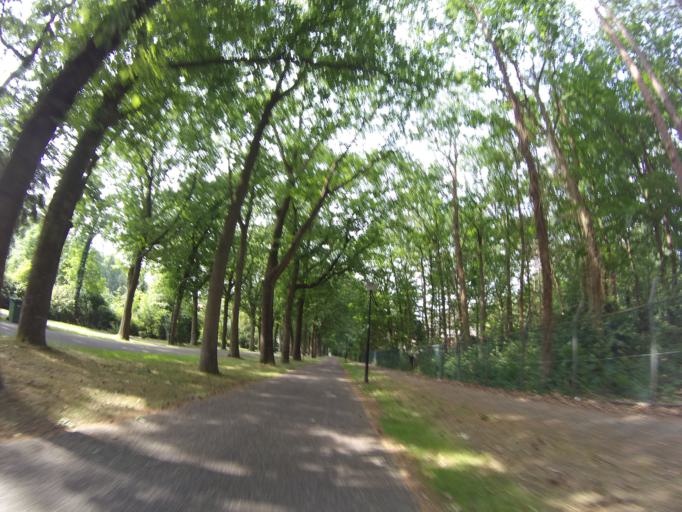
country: NL
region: Utrecht
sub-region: Gemeente Zeist
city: Zeist
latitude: 52.0965
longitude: 5.2595
